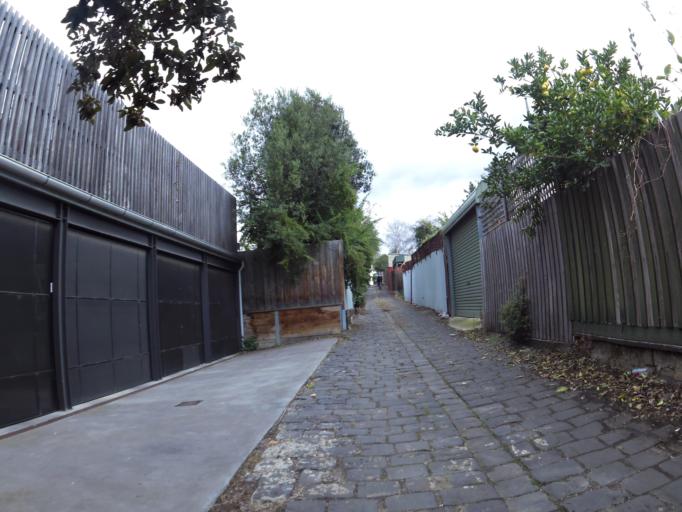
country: AU
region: Victoria
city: Brunswick West
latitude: -37.7628
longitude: 144.9316
